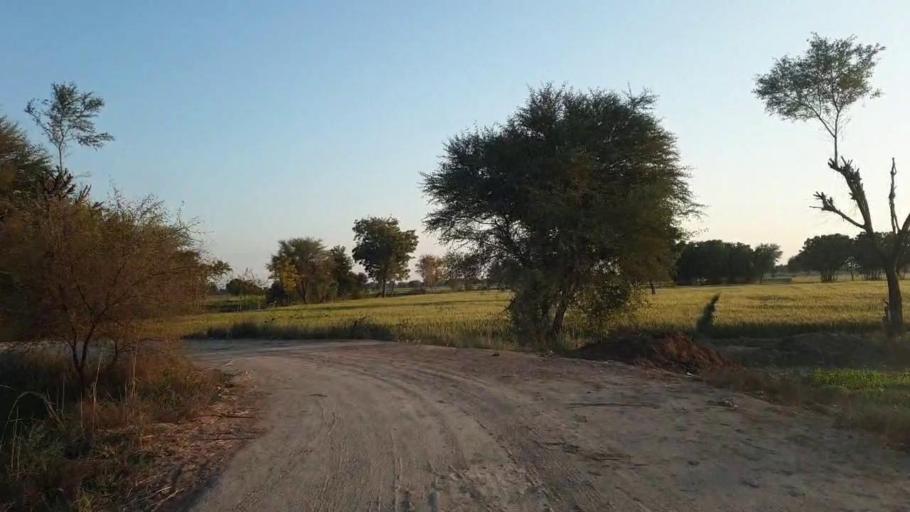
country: PK
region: Sindh
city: Shahpur Chakar
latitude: 26.1508
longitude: 68.5671
